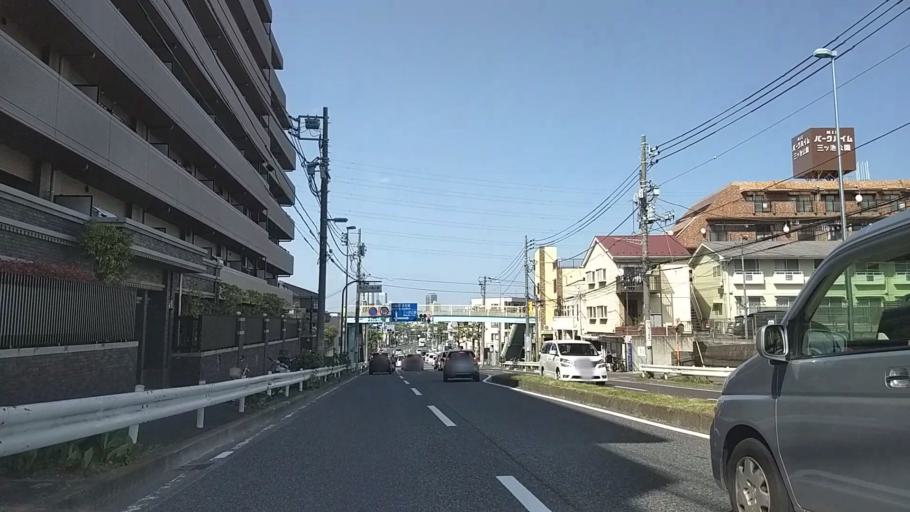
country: JP
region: Kanagawa
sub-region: Kawasaki-shi
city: Kawasaki
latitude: 35.5275
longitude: 139.6610
